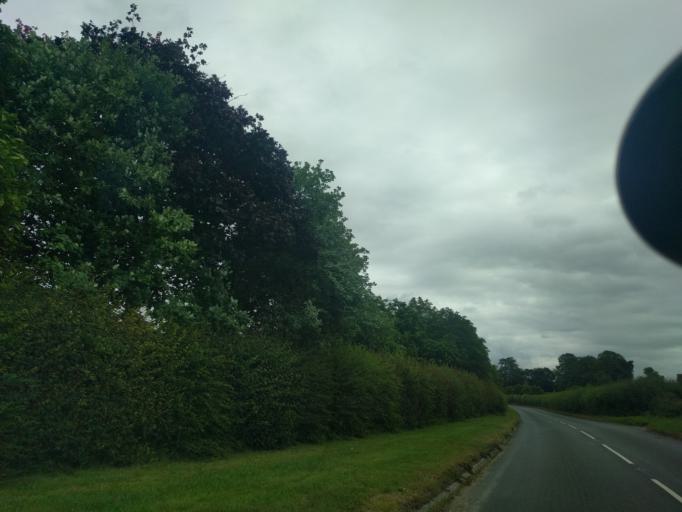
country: GB
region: England
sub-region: Wiltshire
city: Erlestoke
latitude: 51.2800
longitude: -2.0262
